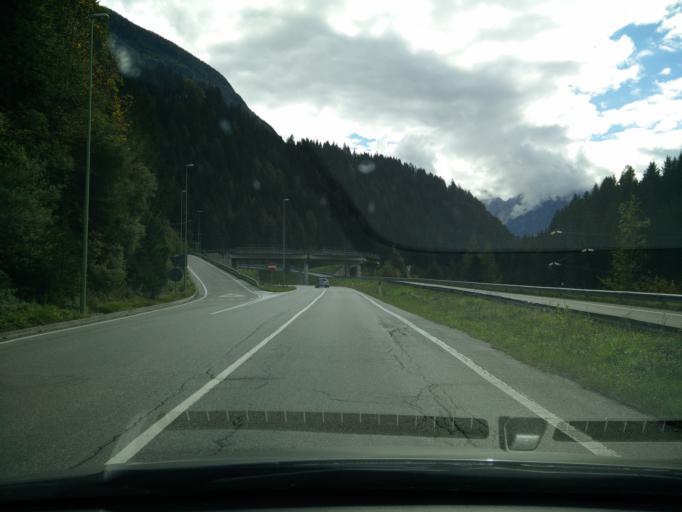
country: IT
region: Veneto
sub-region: Provincia di Belluno
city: Vigo di Cadore
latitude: 46.5346
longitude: 12.4678
